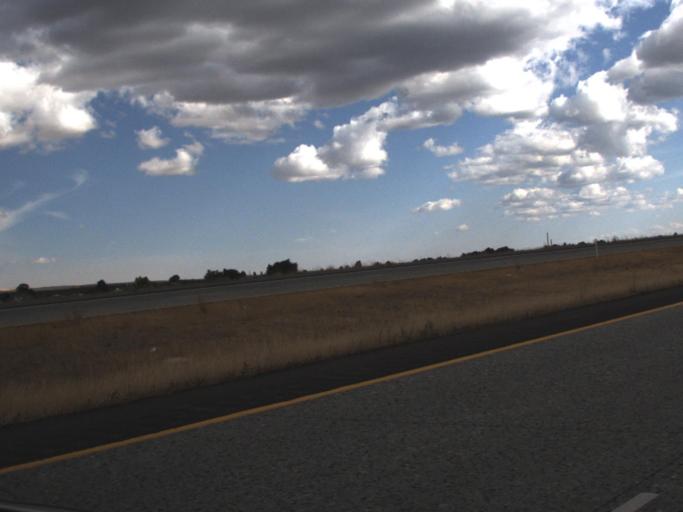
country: US
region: Washington
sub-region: Yakima County
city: Wapato
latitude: 46.4443
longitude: -120.3481
